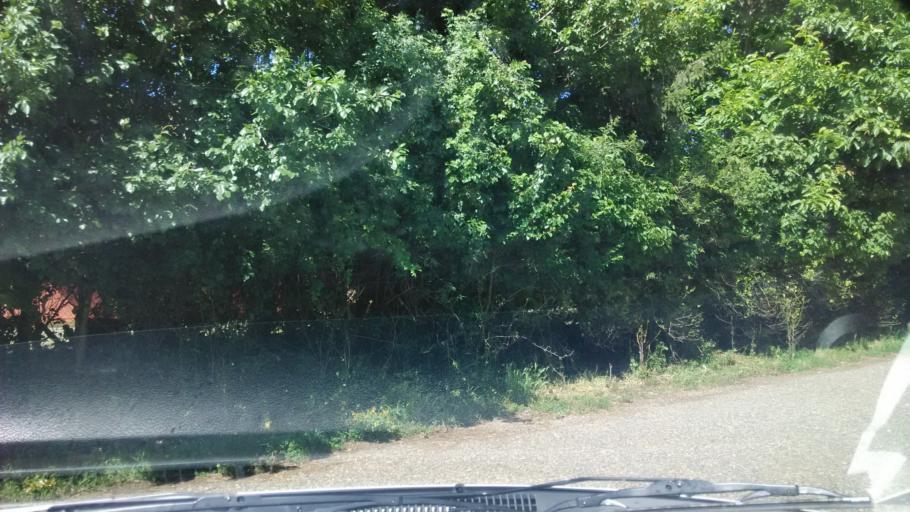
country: SK
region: Nitriansky
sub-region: Okres Nitra
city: Vrable
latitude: 48.1392
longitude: 18.3973
